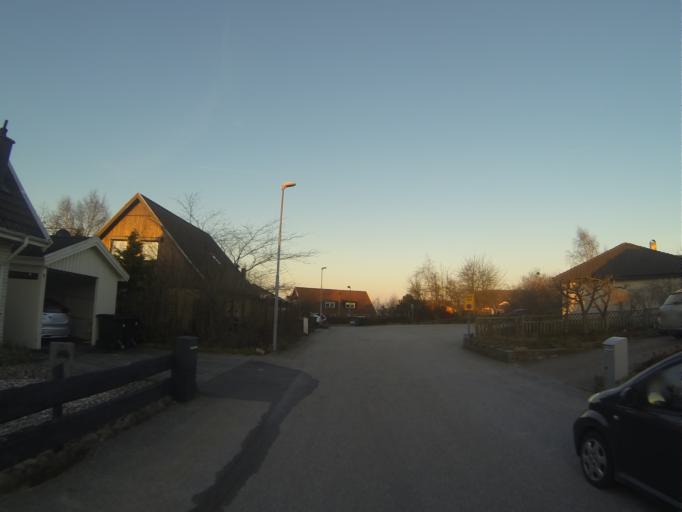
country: SE
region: Skane
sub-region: Lunds Kommun
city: Genarp
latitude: 55.7065
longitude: 13.3387
